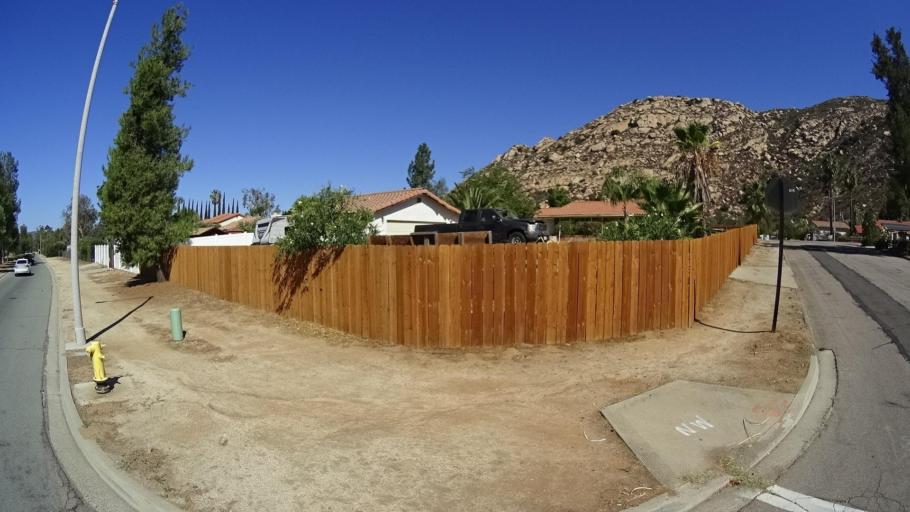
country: US
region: California
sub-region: San Diego County
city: San Diego Country Estates
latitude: 33.0056
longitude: -116.7805
